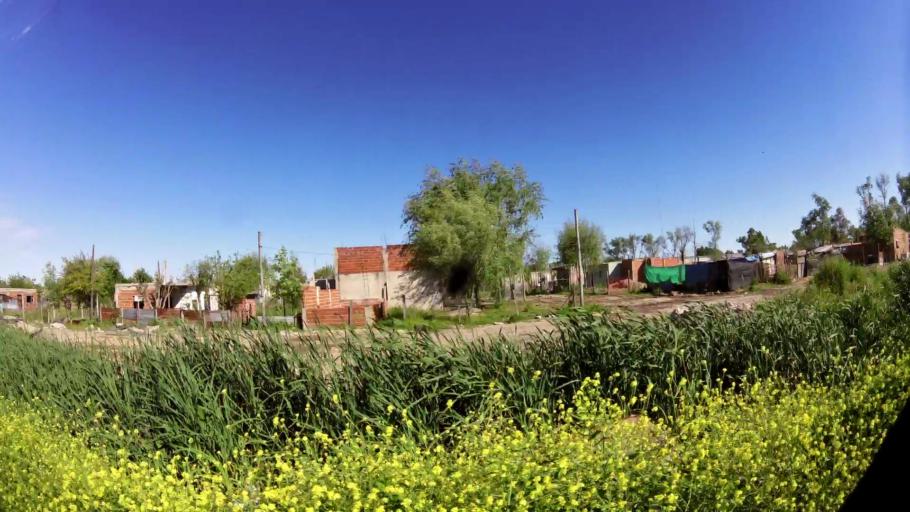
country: AR
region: Buenos Aires
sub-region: Partido de Quilmes
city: Quilmes
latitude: -34.7601
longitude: -58.3127
